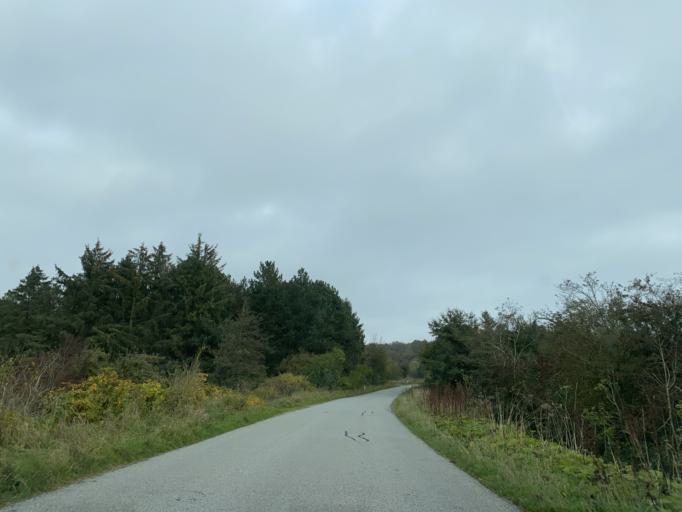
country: DK
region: South Denmark
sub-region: Haderslev Kommune
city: Starup
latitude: 55.1604
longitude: 9.5063
